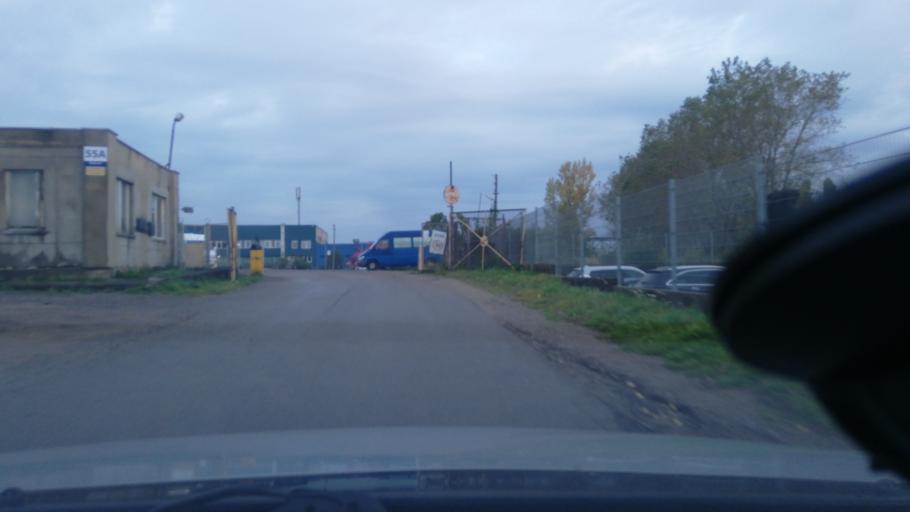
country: LT
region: Klaipedos apskritis
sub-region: Klaipeda
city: Klaipeda
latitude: 55.6873
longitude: 21.1852
